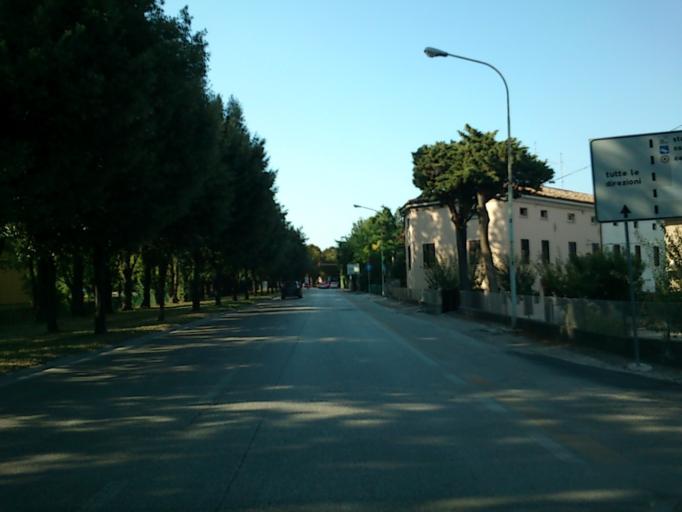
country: IT
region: The Marches
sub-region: Provincia di Pesaro e Urbino
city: Fano
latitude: 43.8358
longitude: 13.0137
